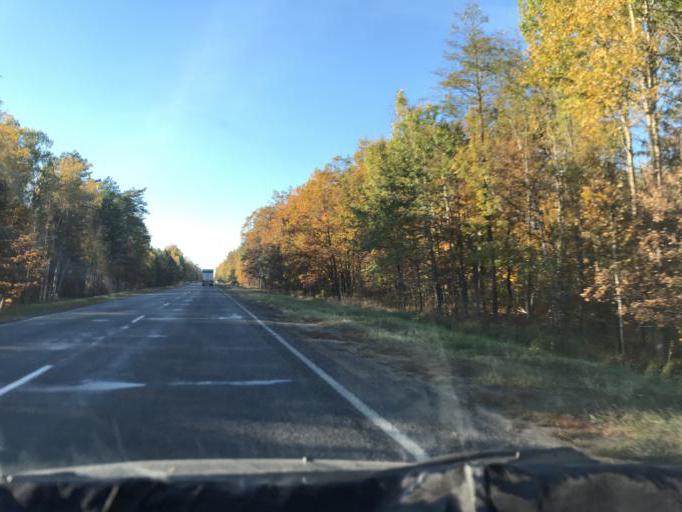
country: BY
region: Gomel
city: Mazyr
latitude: 52.1913
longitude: 29.1227
